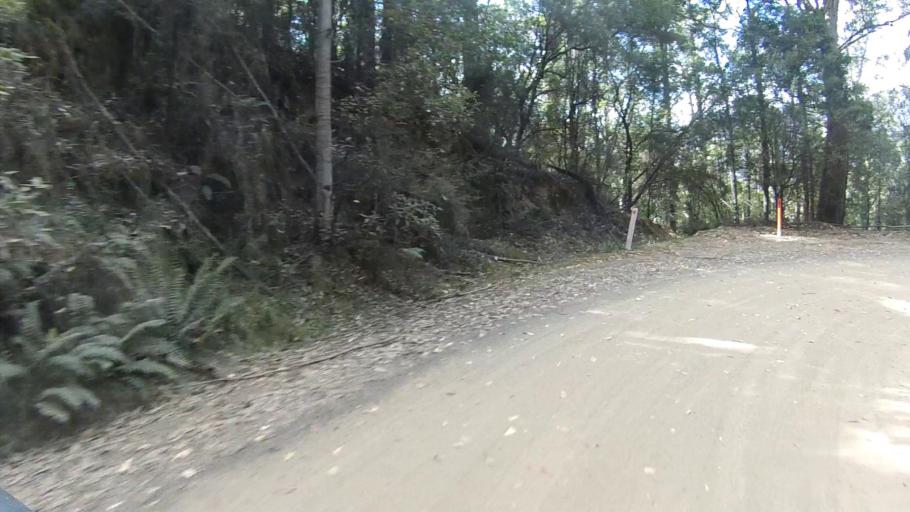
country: AU
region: Tasmania
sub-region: Derwent Valley
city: New Norfolk
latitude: -42.6755
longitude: 146.7047
